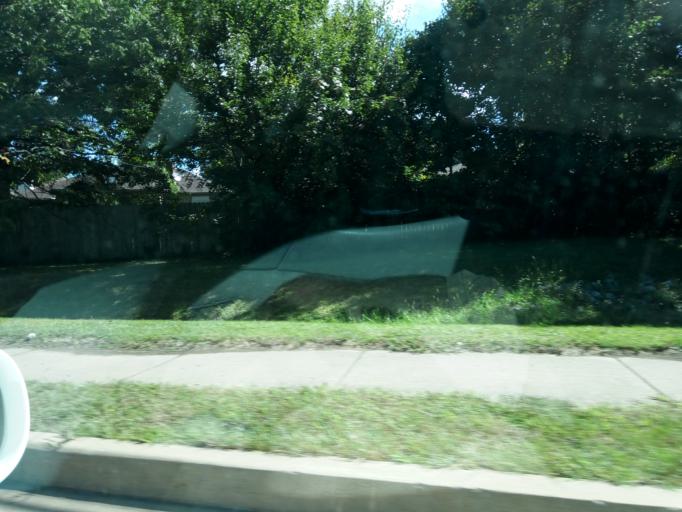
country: US
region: Kentucky
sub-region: Jefferson County
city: Douglass Hills
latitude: 38.2350
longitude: -85.5440
